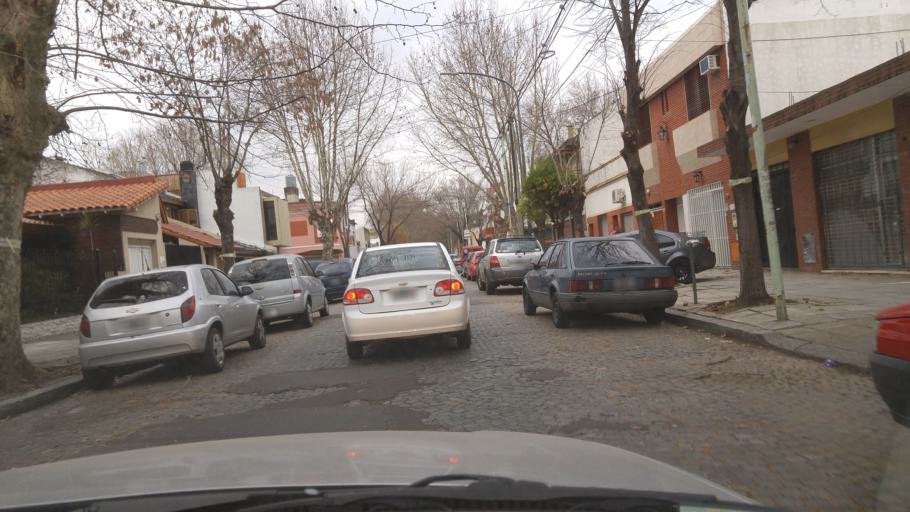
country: AR
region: Buenos Aires F.D.
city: Villa Santa Rita
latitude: -34.6147
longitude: -58.5222
